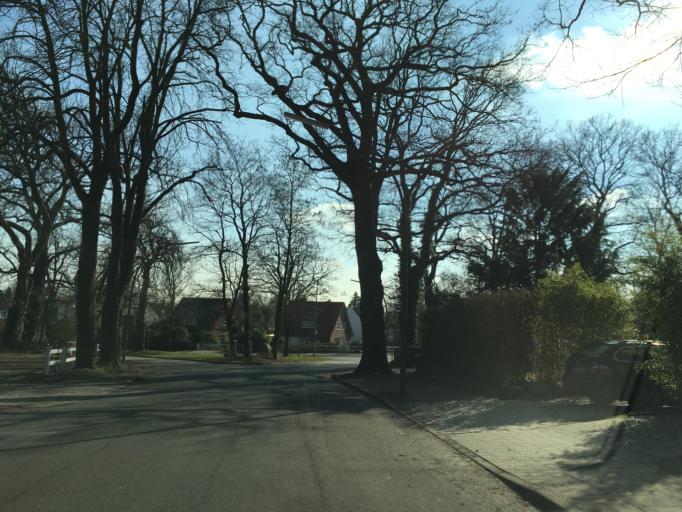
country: DE
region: Hamburg
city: Eidelstedt
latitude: 53.5655
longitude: 9.8735
